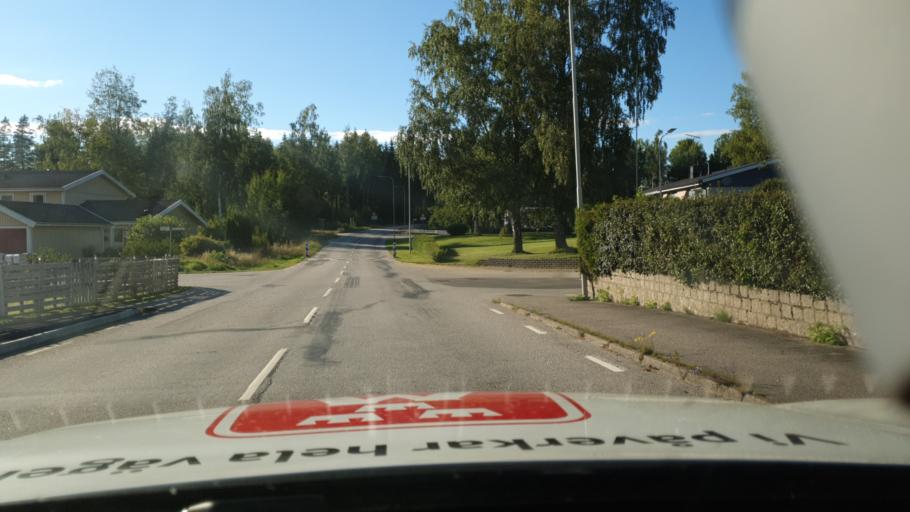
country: SE
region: Vaestra Goetaland
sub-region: Toreboda Kommun
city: Toereboda
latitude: 58.8076
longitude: 14.0577
